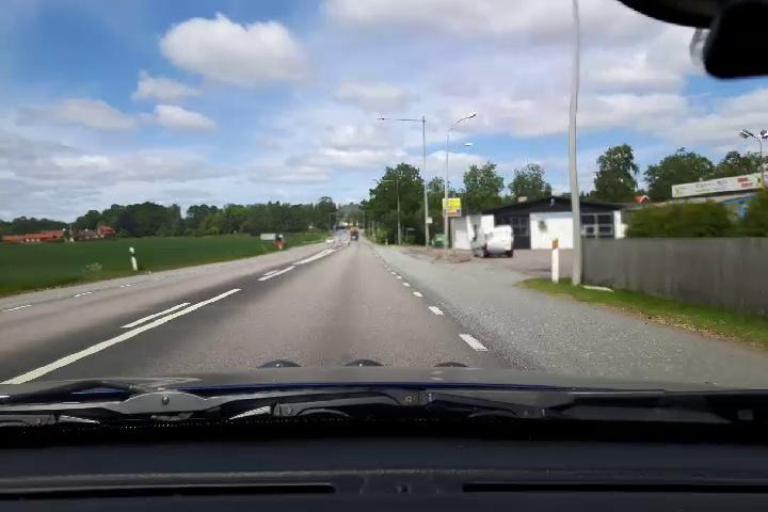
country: SE
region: Uppsala
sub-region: Osthammars Kommun
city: Bjorklinge
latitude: 60.0226
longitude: 17.5545
